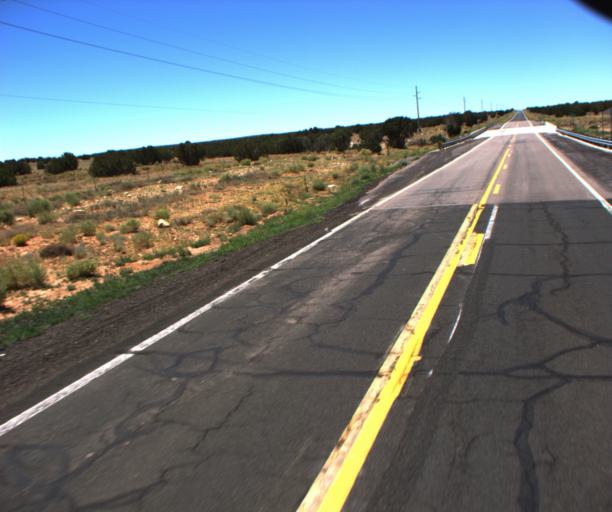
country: US
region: Arizona
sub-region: Coconino County
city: LeChee
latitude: 34.8501
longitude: -110.9281
